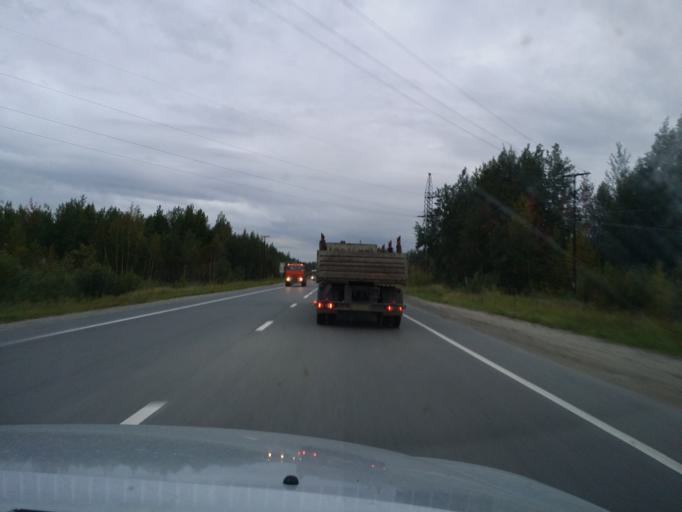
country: RU
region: Khanty-Mansiyskiy Avtonomnyy Okrug
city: Izluchinsk
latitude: 61.0085
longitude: 76.7684
